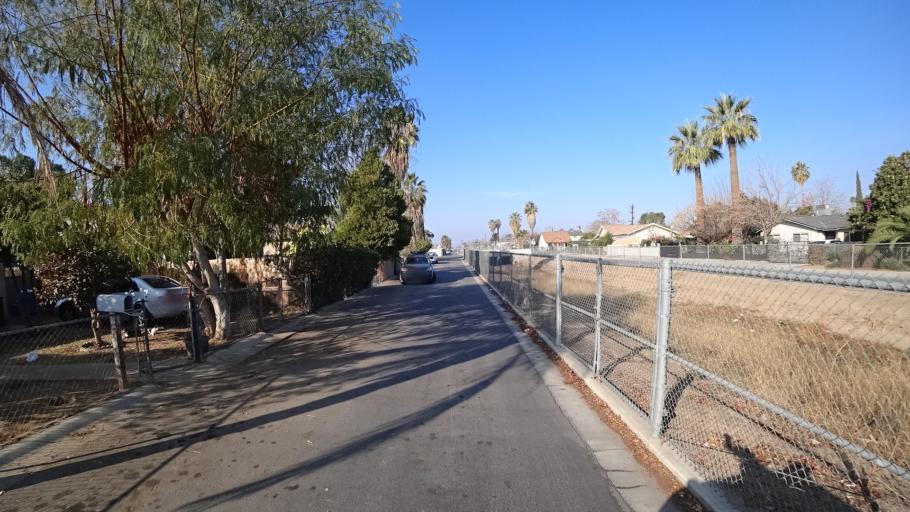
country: US
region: California
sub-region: Kern County
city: Bakersfield
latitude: 35.3767
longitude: -118.9786
